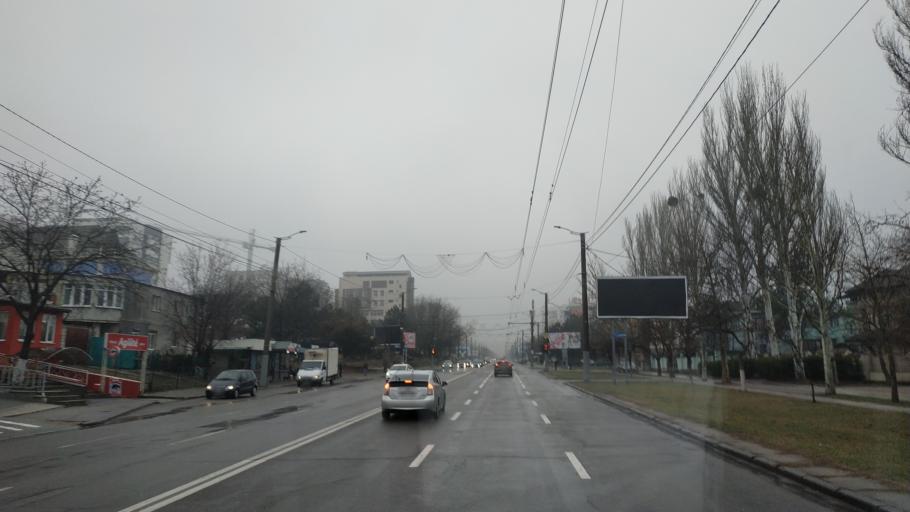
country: MD
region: Chisinau
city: Vatra
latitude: 47.0317
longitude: 28.7835
